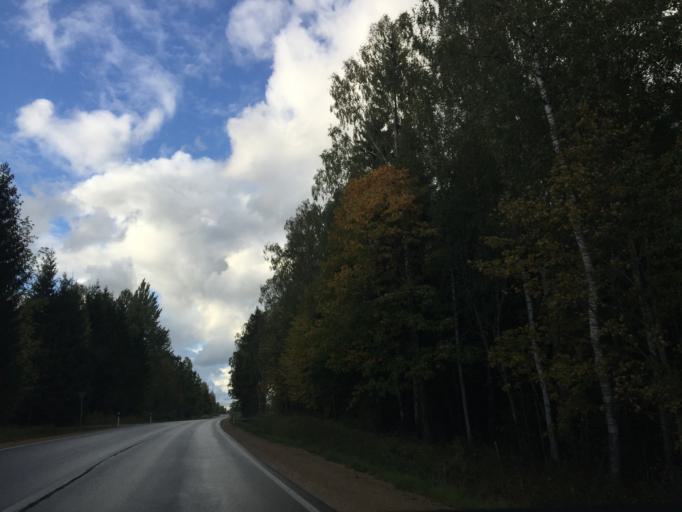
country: LV
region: Ligatne
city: Ligatne
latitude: 57.1663
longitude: 25.0480
